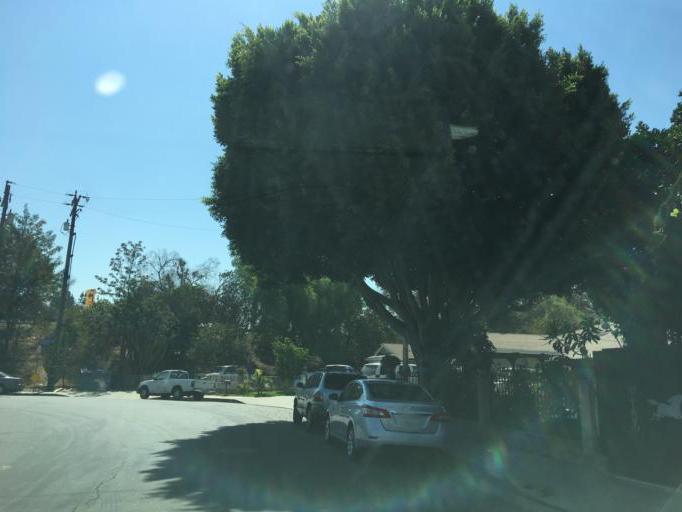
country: US
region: California
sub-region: Los Angeles County
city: South El Monte
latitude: 34.0336
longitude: -118.0304
